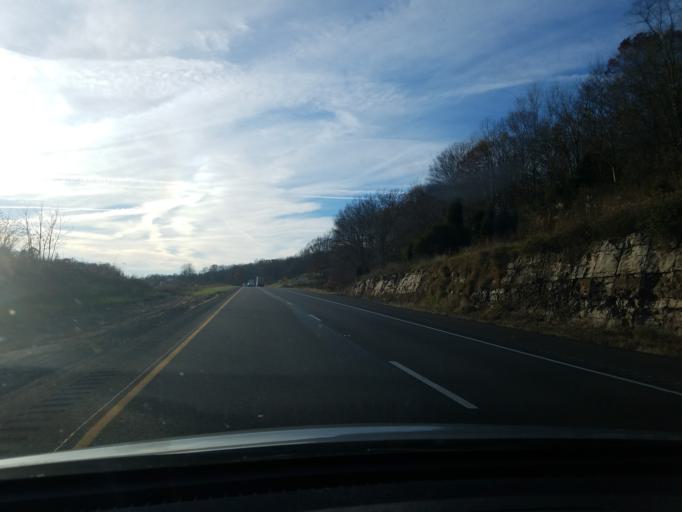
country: US
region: Indiana
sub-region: Crawford County
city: English
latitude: 38.2384
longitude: -86.4818
